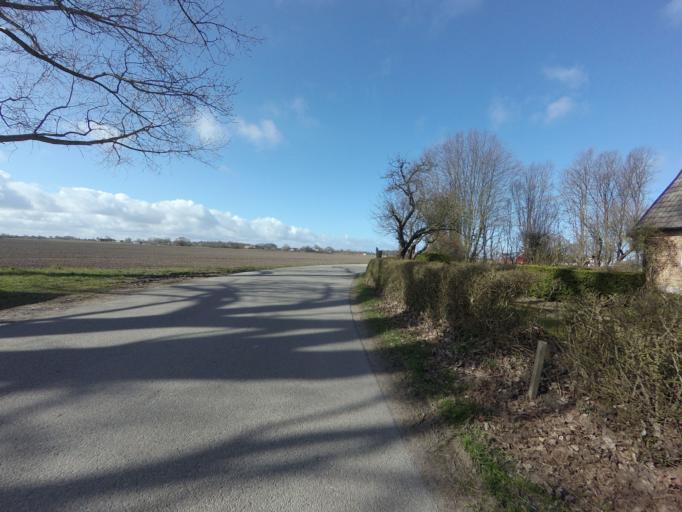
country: SE
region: Skane
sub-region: Hoganas Kommun
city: Hoganas
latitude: 56.1845
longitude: 12.6143
